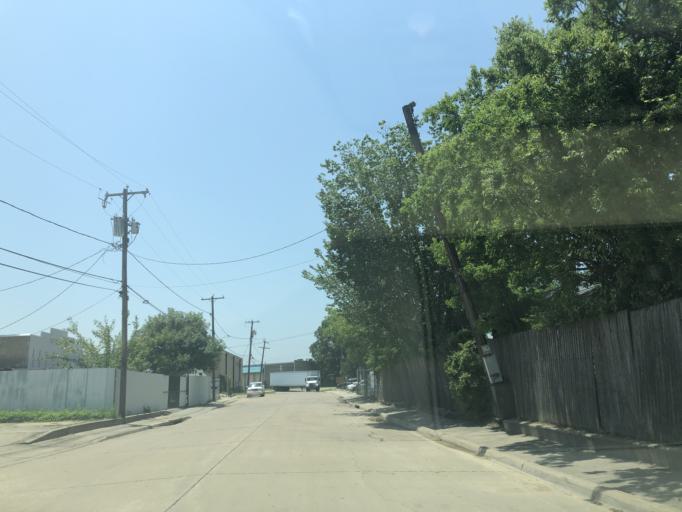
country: US
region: Texas
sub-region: Dallas County
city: Dallas
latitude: 32.8027
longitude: -96.8474
